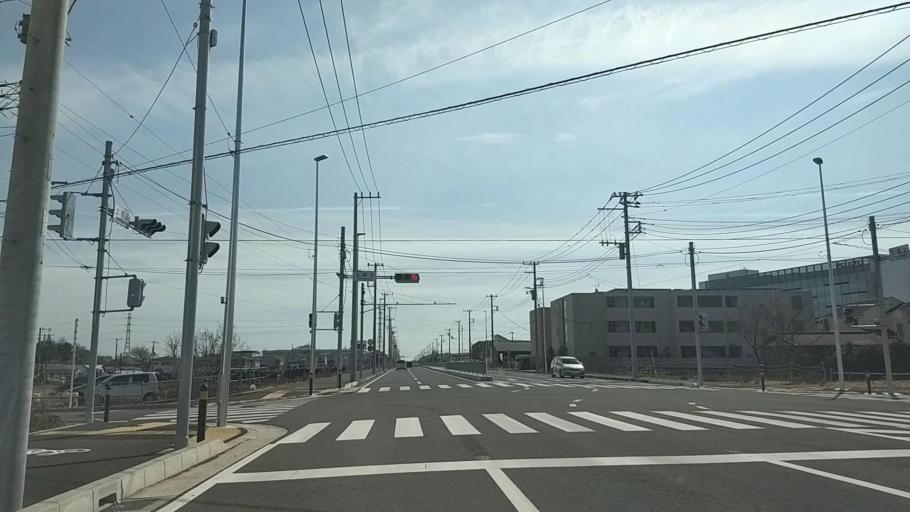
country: JP
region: Kanagawa
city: Fujisawa
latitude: 35.4055
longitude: 139.4542
